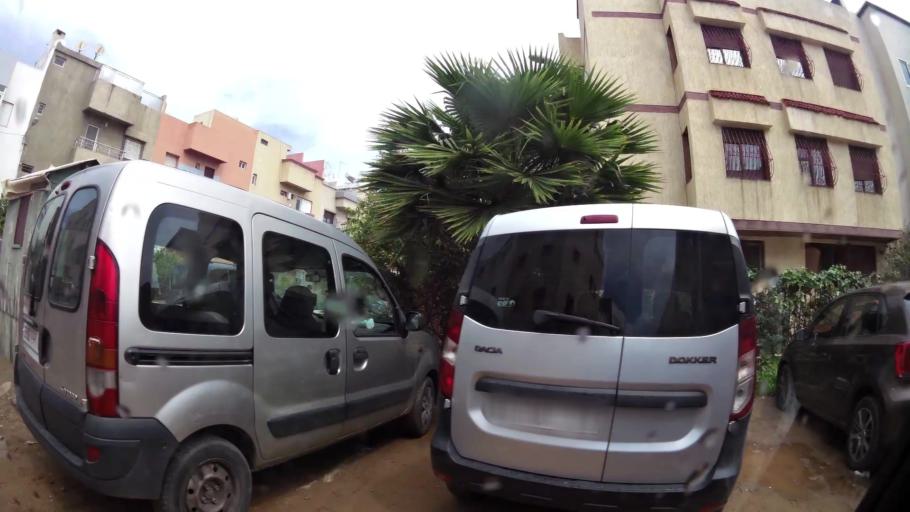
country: MA
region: Grand Casablanca
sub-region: Casablanca
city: Casablanca
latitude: 33.5508
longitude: -7.6879
